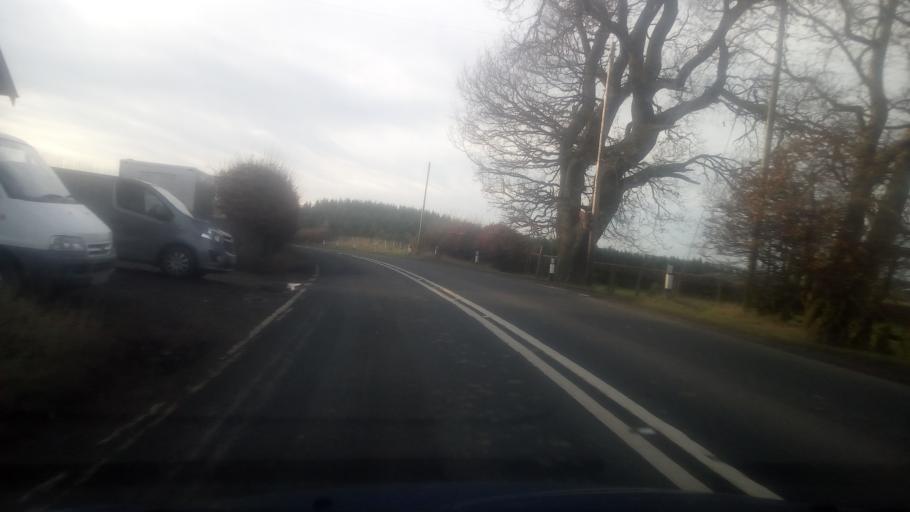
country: GB
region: Scotland
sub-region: The Scottish Borders
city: Jedburgh
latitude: 55.4212
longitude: -2.5224
